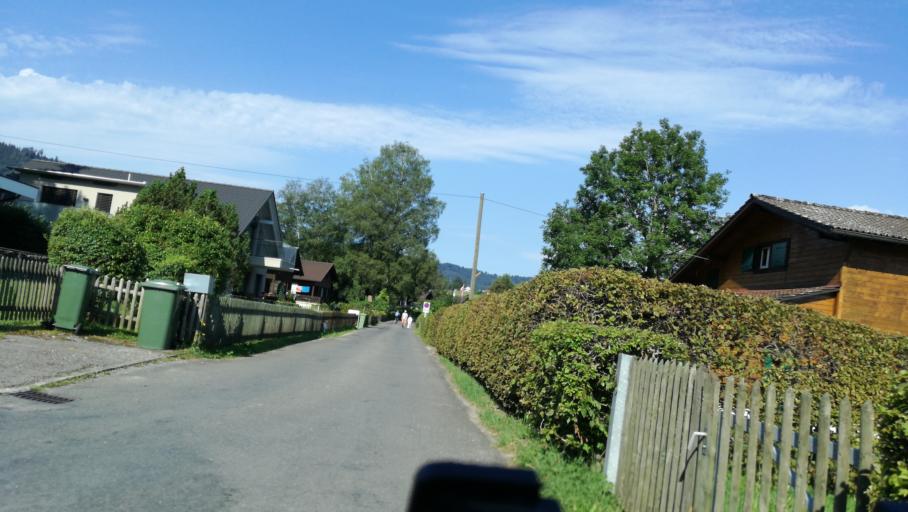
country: CH
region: Zug
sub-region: Zug
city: Unterageri
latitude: 47.1220
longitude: 8.5936
